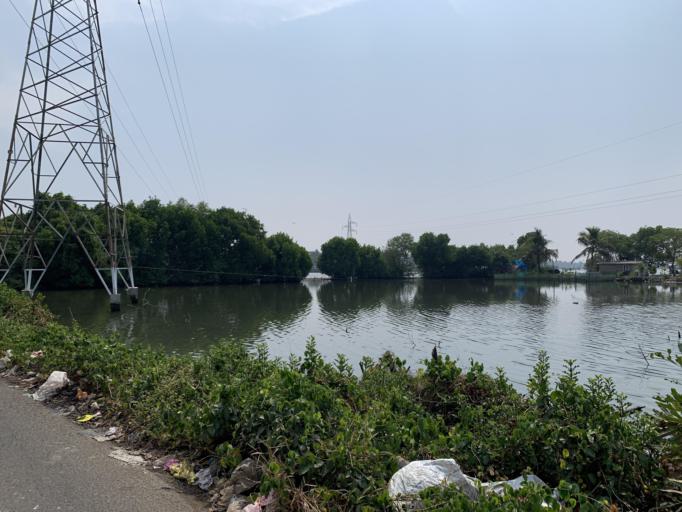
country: IN
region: Kerala
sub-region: Ernakulam
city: Cochin
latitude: 9.9137
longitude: 76.2653
